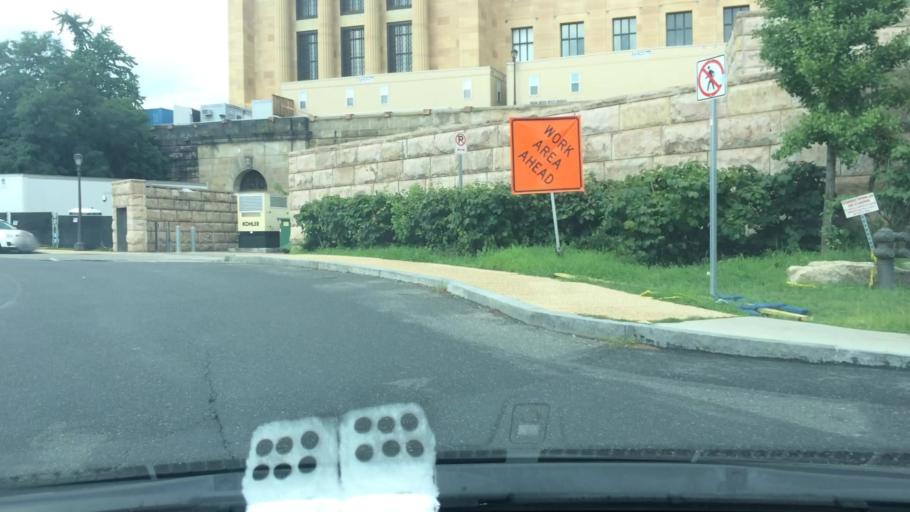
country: US
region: Pennsylvania
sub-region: Philadelphia County
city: Philadelphia
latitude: 39.9646
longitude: -75.1822
